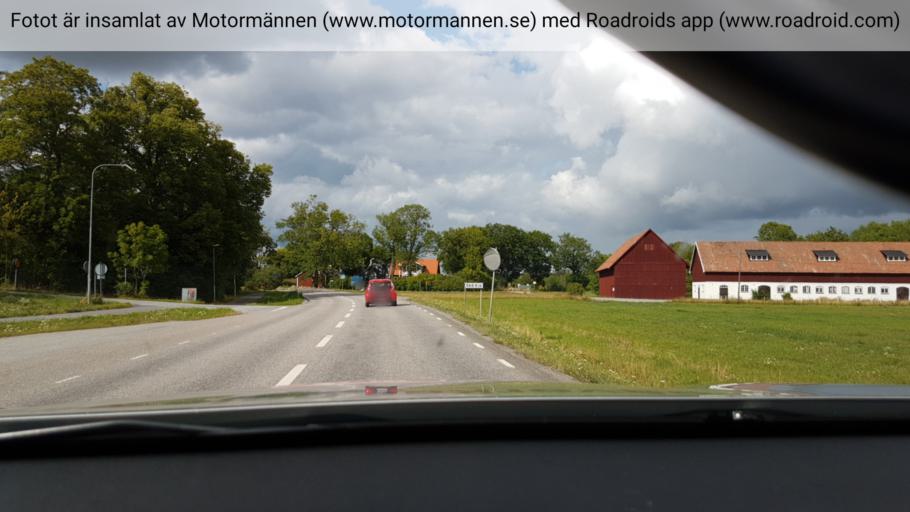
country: SE
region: Stockholm
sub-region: Ekero Kommun
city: Ekeroe
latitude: 59.3316
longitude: 17.7463
